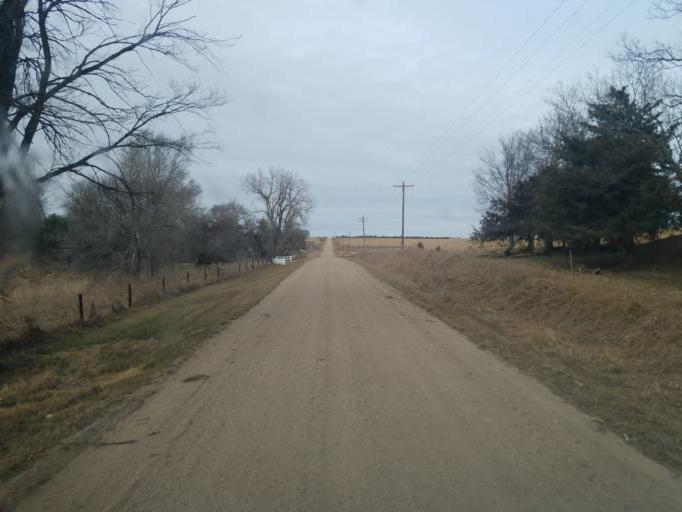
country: US
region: Nebraska
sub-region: Holt County
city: O'Neill
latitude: 42.4435
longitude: -98.3055
